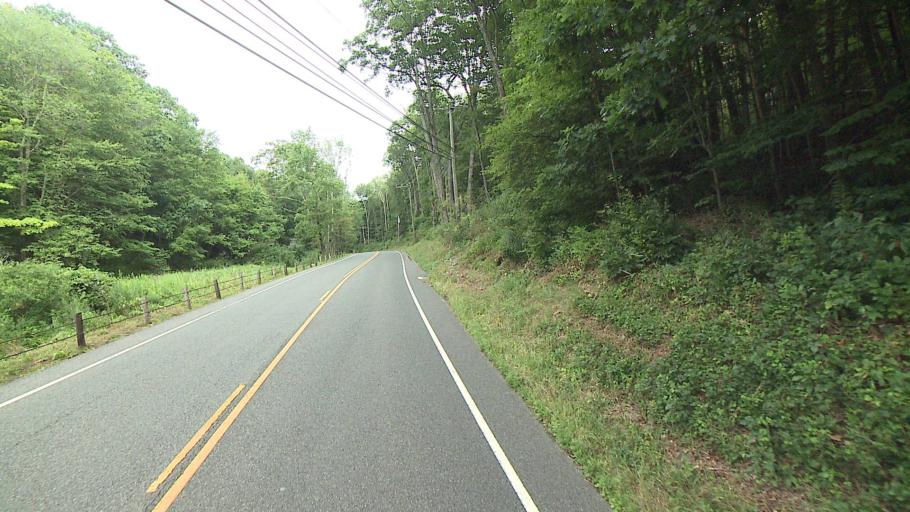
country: US
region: Connecticut
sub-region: Litchfield County
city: New Preston
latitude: 41.6218
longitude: -73.2973
